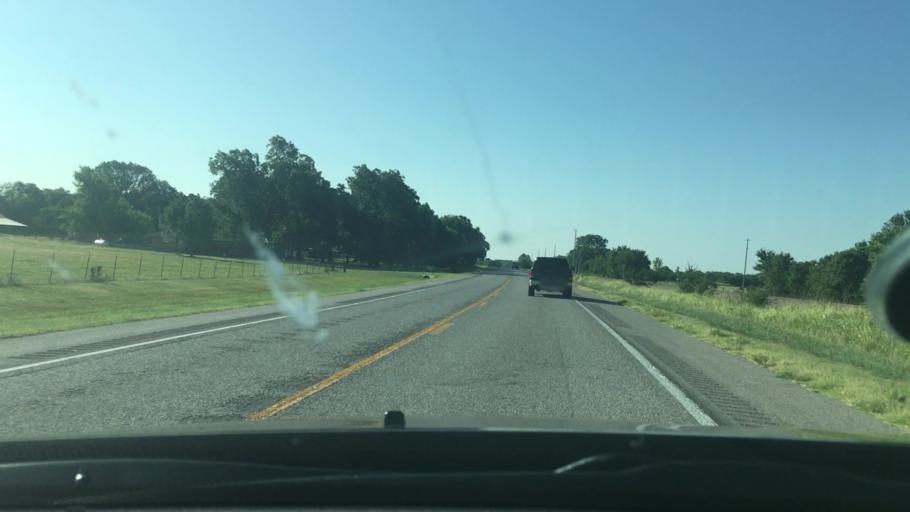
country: US
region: Oklahoma
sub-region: Johnston County
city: Tishomingo
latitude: 34.2613
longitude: -96.7698
